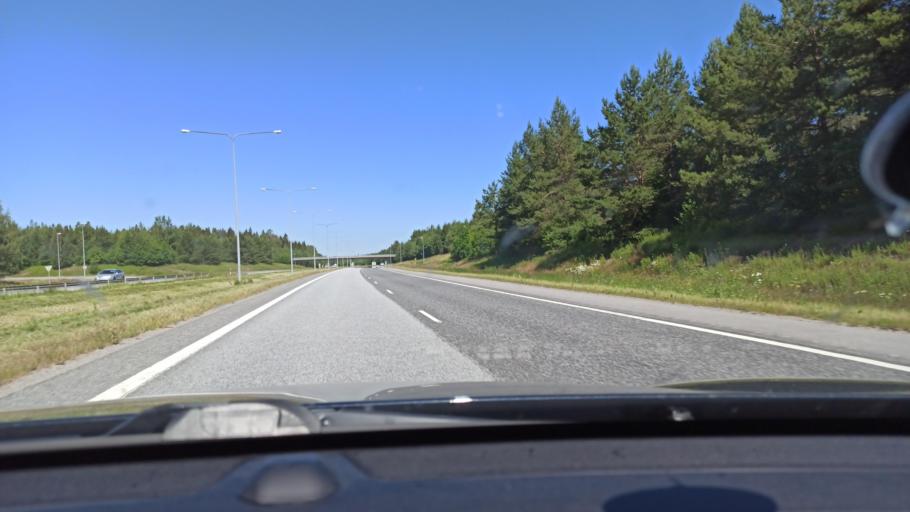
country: FI
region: Ostrobothnia
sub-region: Vaasa
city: Ristinummi
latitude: 63.0541
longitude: 21.7142
